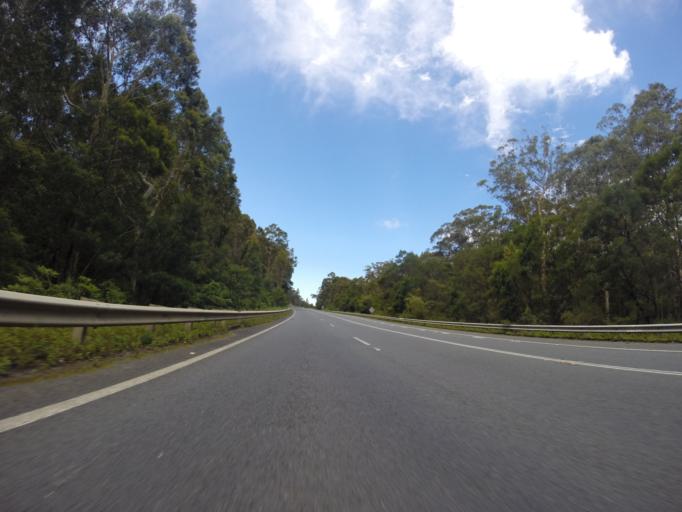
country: AU
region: New South Wales
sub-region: Shoalhaven Shire
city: Falls Creek
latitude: -35.0769
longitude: 150.5565
